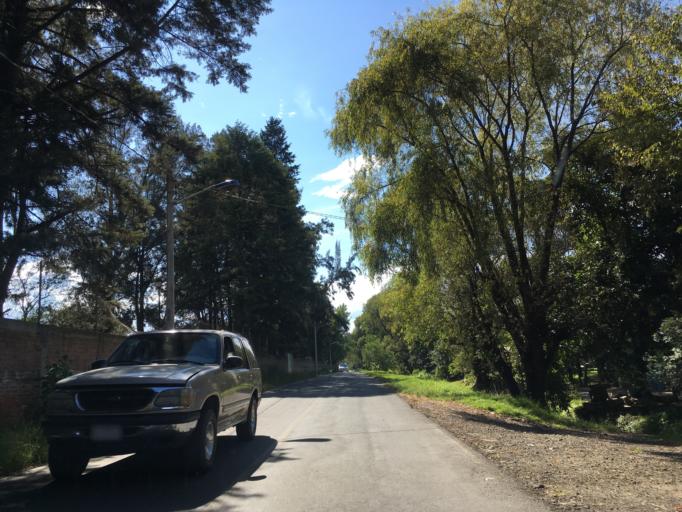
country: MX
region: Michoacan
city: Zacapu
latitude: 19.8241
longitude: -101.7773
